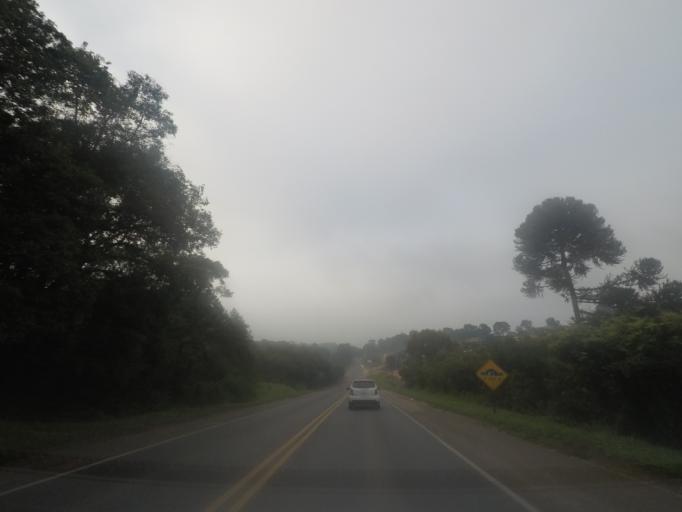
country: BR
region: Parana
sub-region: Almirante Tamandare
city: Almirante Tamandare
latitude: -25.2910
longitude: -49.3050
